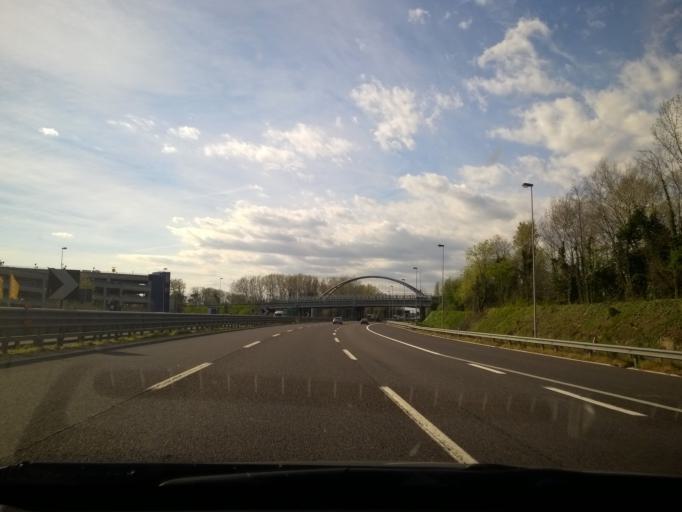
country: IT
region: Veneto
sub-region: Provincia di Padova
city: Noventa
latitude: 45.4201
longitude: 11.9367
